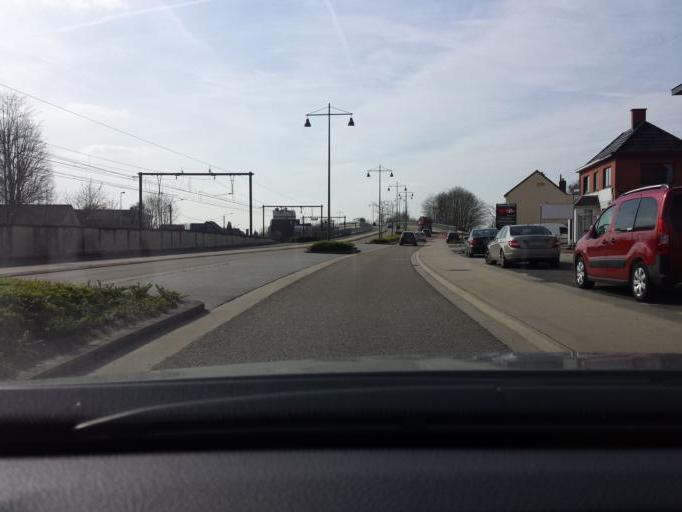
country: BE
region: Flanders
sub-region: Provincie Limburg
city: Hasselt
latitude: 50.9442
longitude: 5.2743
